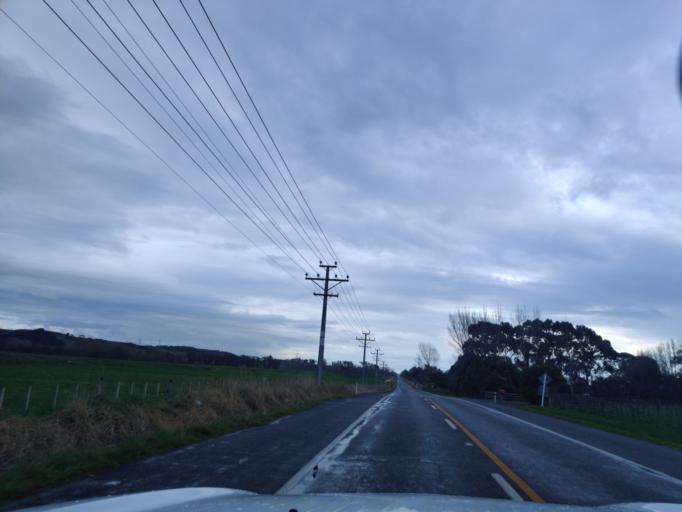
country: NZ
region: Manawatu-Wanganui
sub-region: Palmerston North City
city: Palmerston North
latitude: -40.3388
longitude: 175.7217
